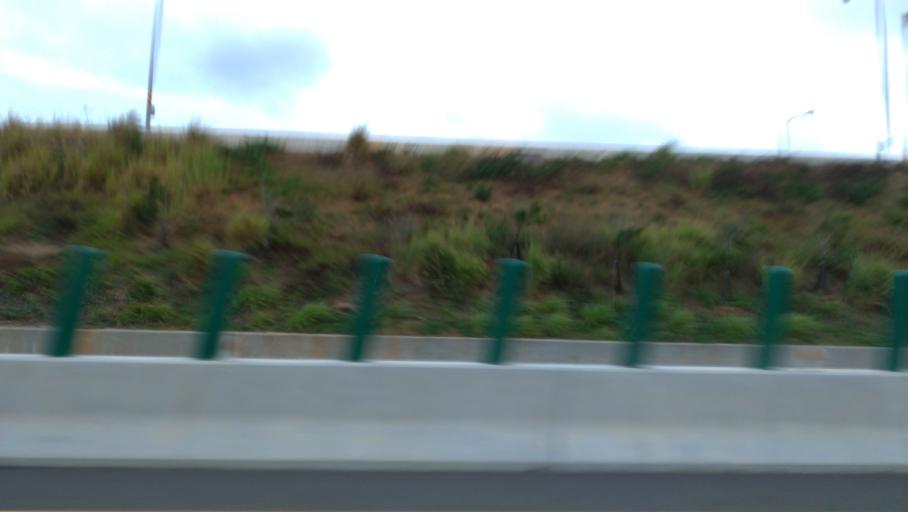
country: TW
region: Taiwan
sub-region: Miaoli
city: Miaoli
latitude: 24.5431
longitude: 120.7017
